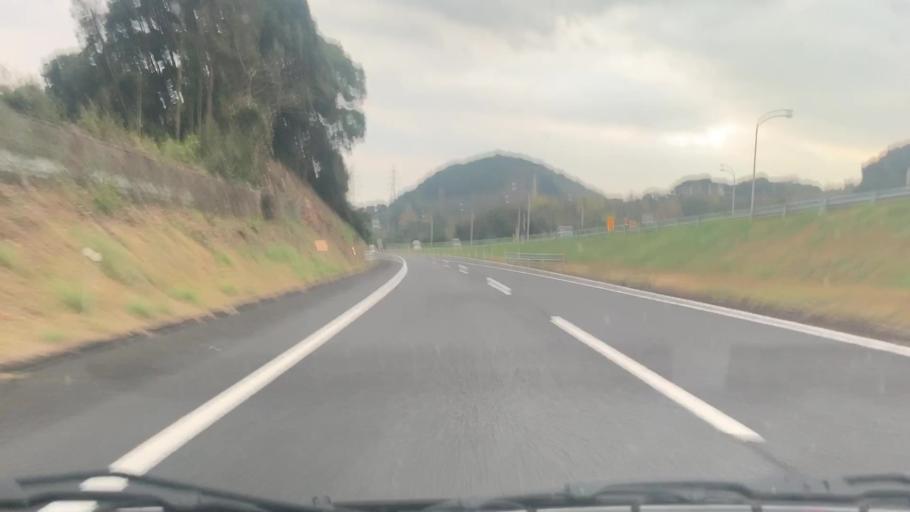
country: JP
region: Nagasaki
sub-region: Isahaya-shi
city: Isahaya
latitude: 32.8613
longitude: 130.0019
